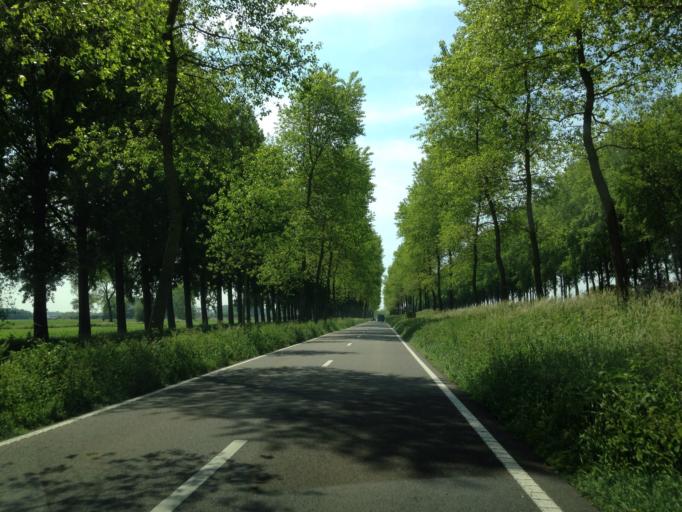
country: BE
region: Flanders
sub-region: Provincie West-Vlaanderen
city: Damme
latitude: 51.2414
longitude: 3.2680
